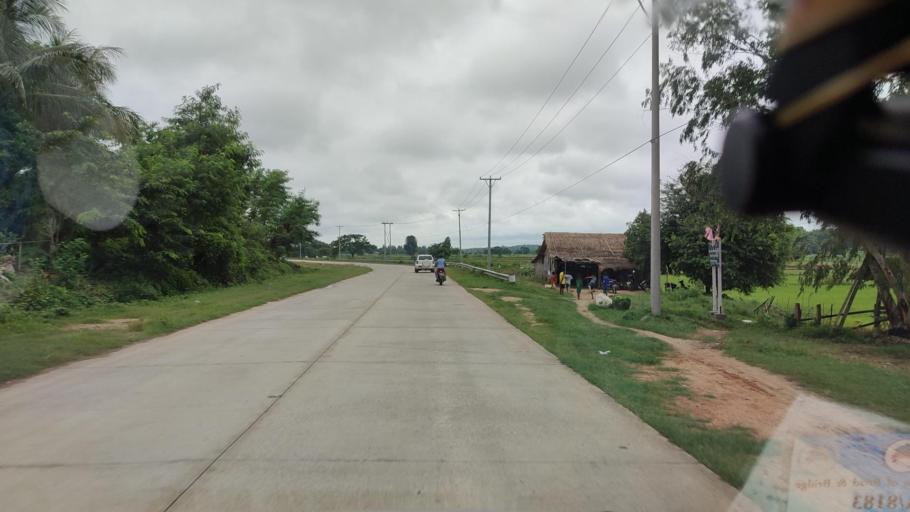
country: MM
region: Mandalay
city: Nay Pyi Taw
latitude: 19.8592
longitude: 96.0285
